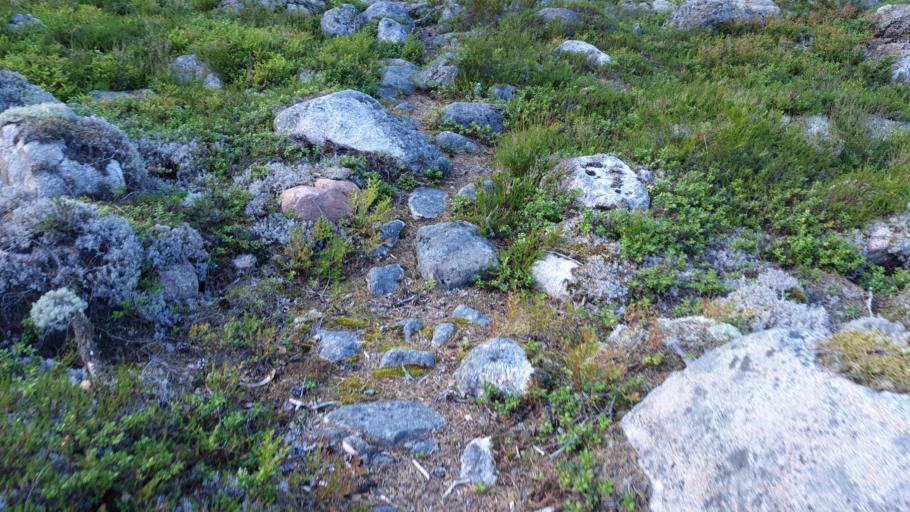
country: SE
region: Gaevleborg
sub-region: Soderhamns Kommun
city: Marielund
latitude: 61.4234
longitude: 17.1534
